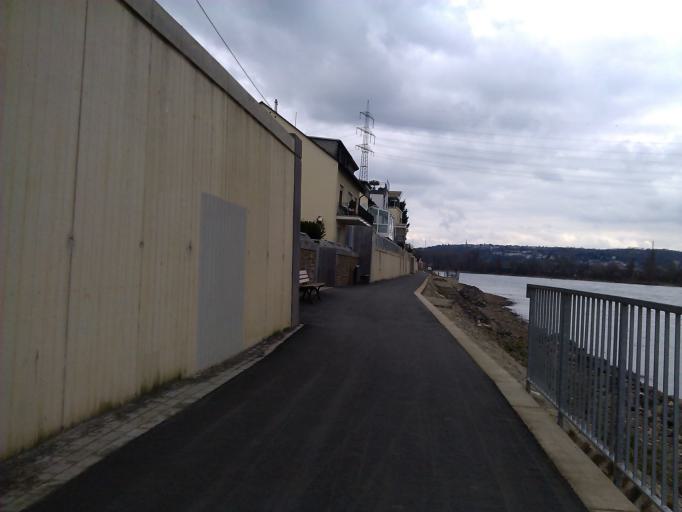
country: DE
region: Rheinland-Pfalz
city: Niederwerth
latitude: 50.3813
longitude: 7.6110
